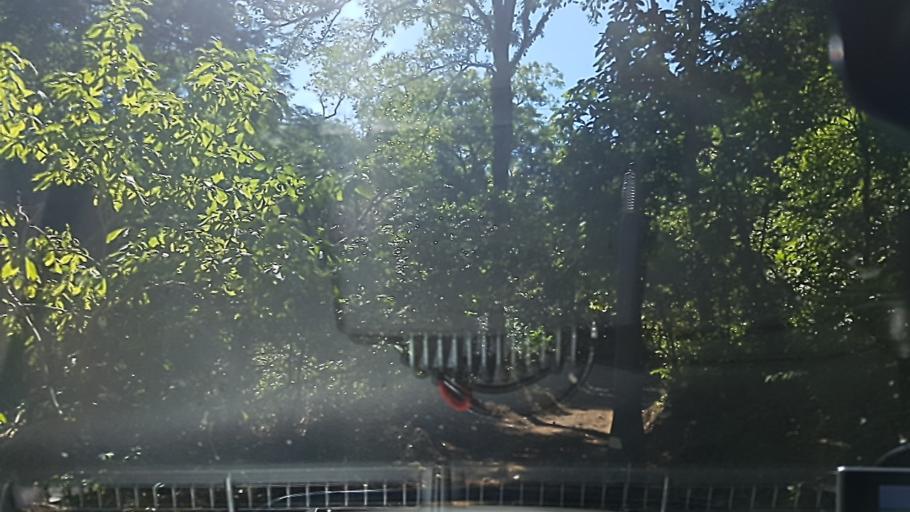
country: NI
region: Rivas
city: Tola
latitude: 11.5518
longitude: -86.0897
